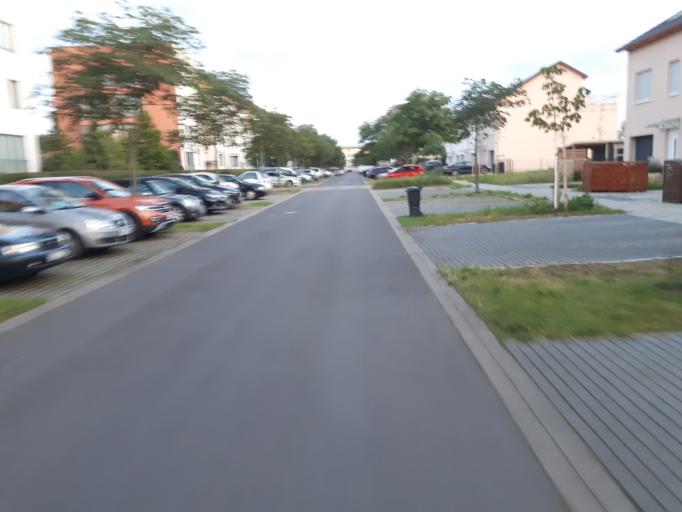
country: DE
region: Berlin
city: Staaken
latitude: 52.5621
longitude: 13.1366
